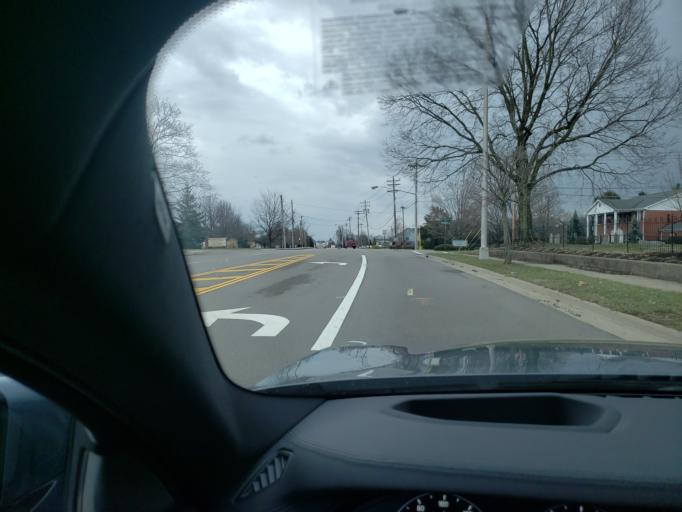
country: US
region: Ohio
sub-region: Hamilton County
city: Springdale
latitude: 39.2810
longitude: -84.4849
